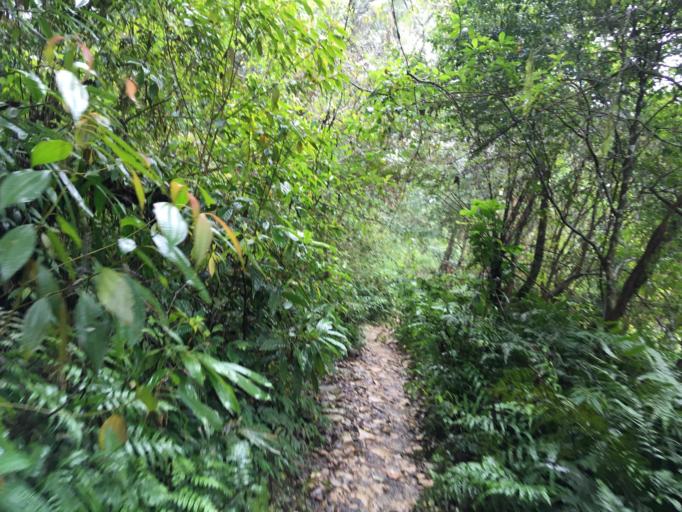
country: TW
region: Taiwan
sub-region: Yilan
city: Yilan
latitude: 24.6772
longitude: 121.5705
